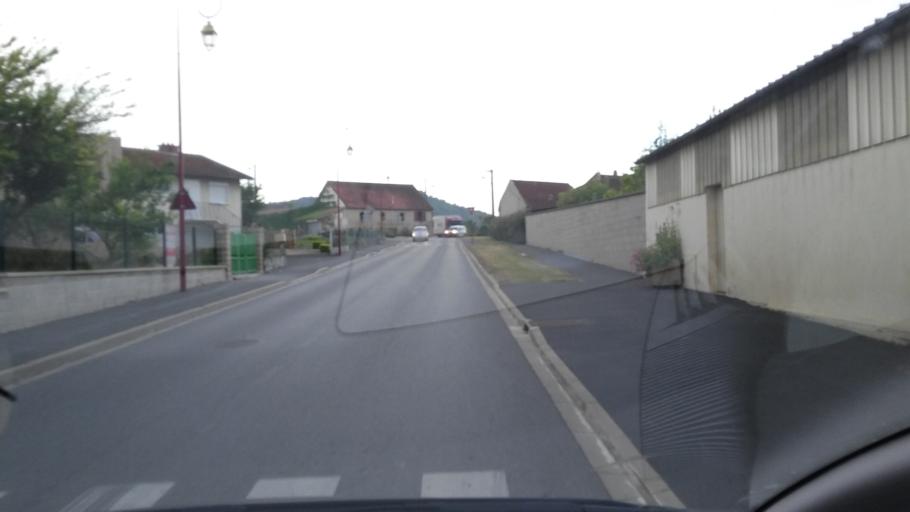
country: FR
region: Champagne-Ardenne
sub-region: Departement de la Marne
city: Vertus
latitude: 48.8771
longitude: 4.0003
